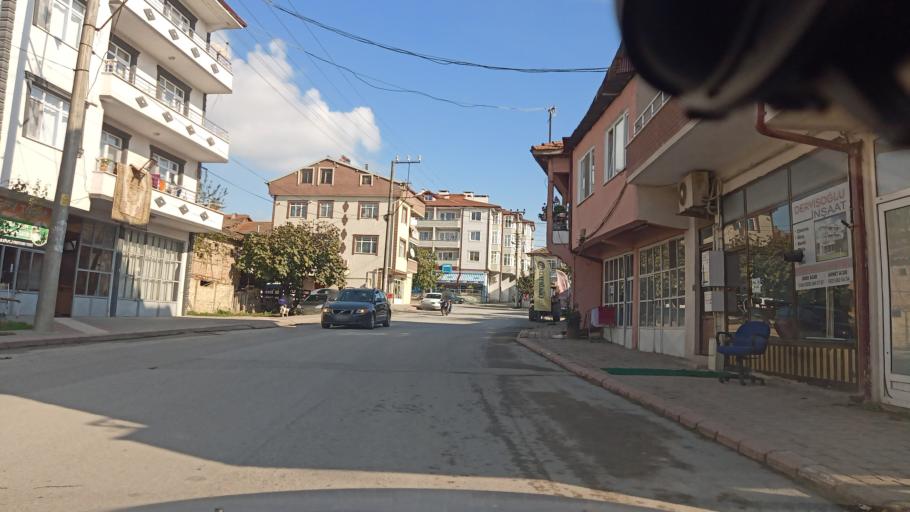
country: TR
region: Sakarya
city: Kaynarca
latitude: 41.0306
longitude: 30.3069
